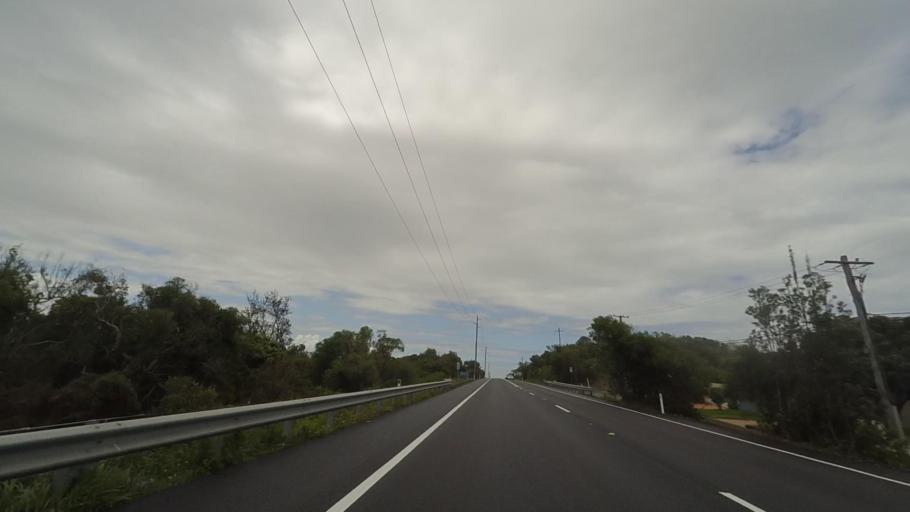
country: AU
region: New South Wales
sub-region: Wyong Shire
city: The Entrance
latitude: -33.3244
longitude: 151.5127
